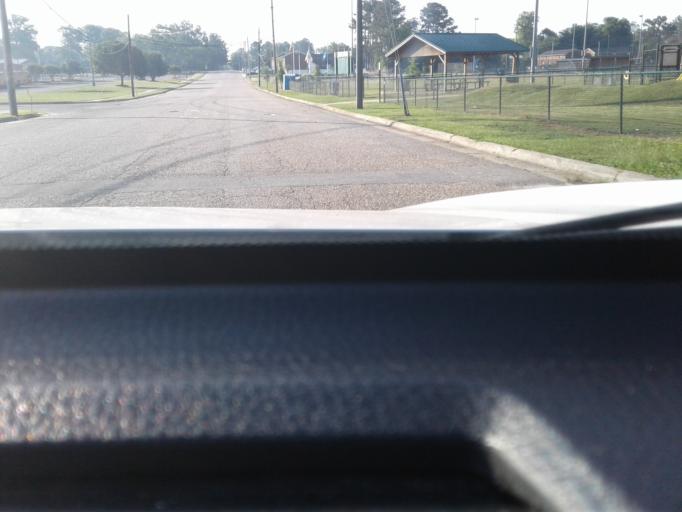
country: US
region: North Carolina
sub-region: Harnett County
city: Dunn
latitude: 35.3151
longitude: -78.6180
